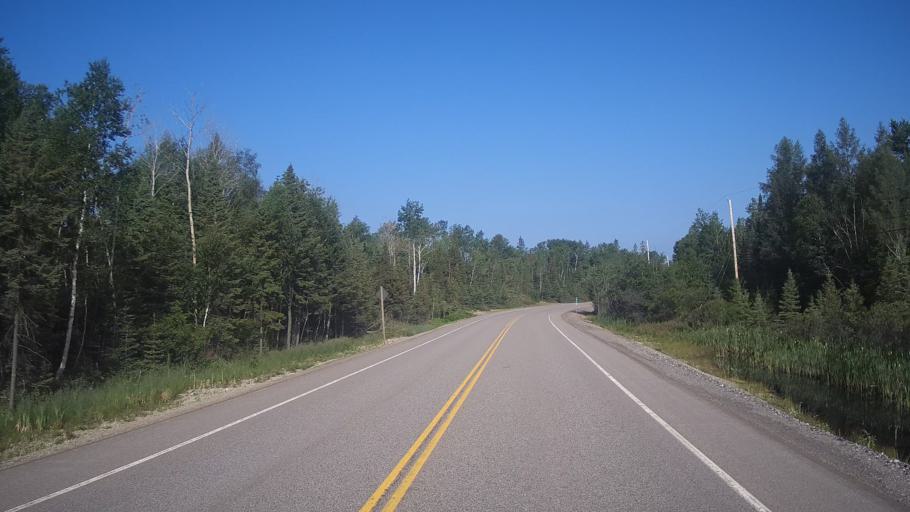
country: CA
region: Ontario
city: Rayside-Balfour
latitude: 46.7312
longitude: -81.5862
